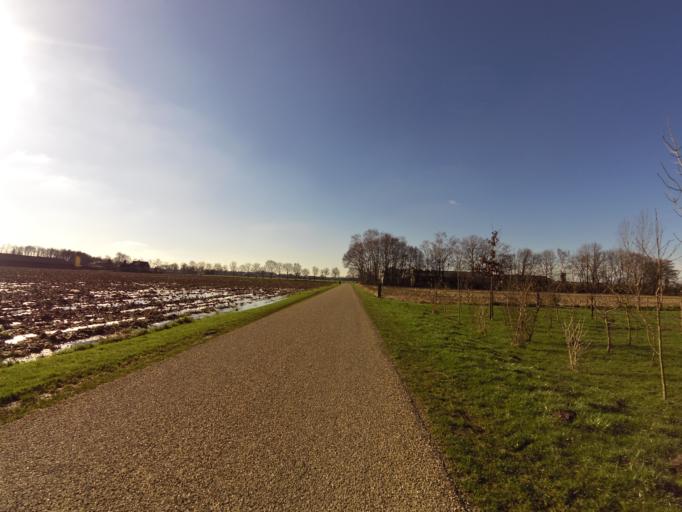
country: NL
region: Gelderland
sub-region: Gemeente Doetinchem
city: Doetinchem
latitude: 51.9617
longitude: 6.2357
